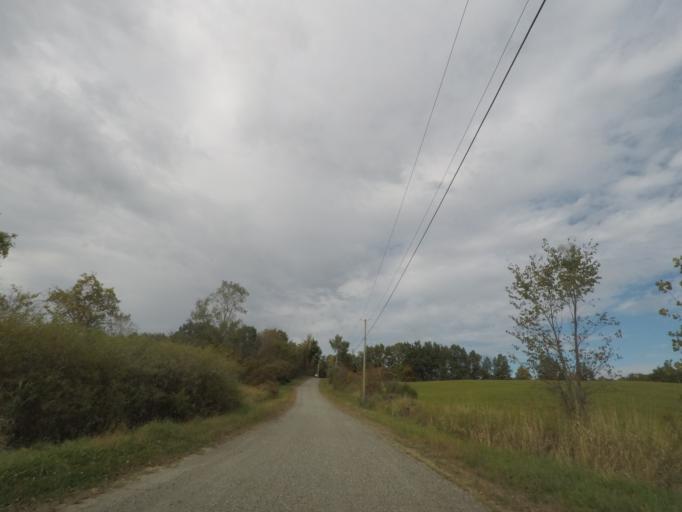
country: US
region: New York
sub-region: Rensselaer County
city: West Sand Lake
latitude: 42.5799
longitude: -73.6129
